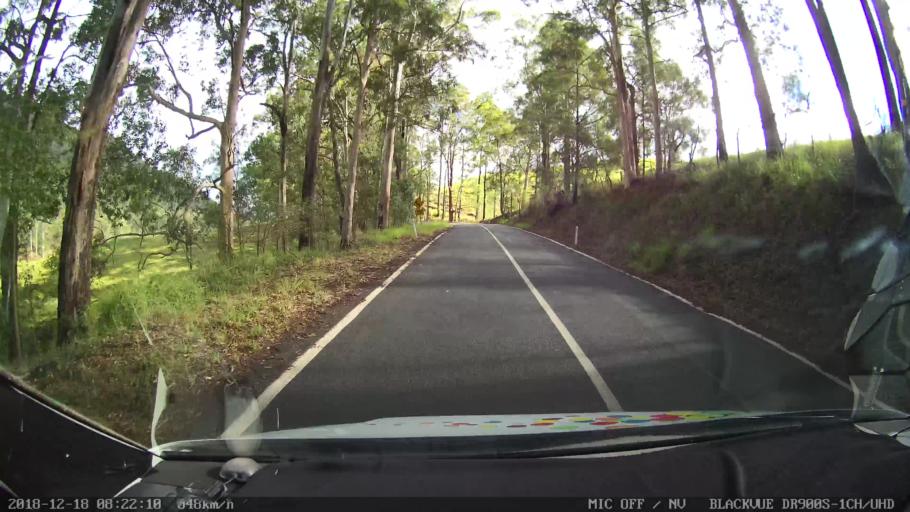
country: AU
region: New South Wales
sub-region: Kyogle
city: Kyogle
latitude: -28.3269
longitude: 152.7247
